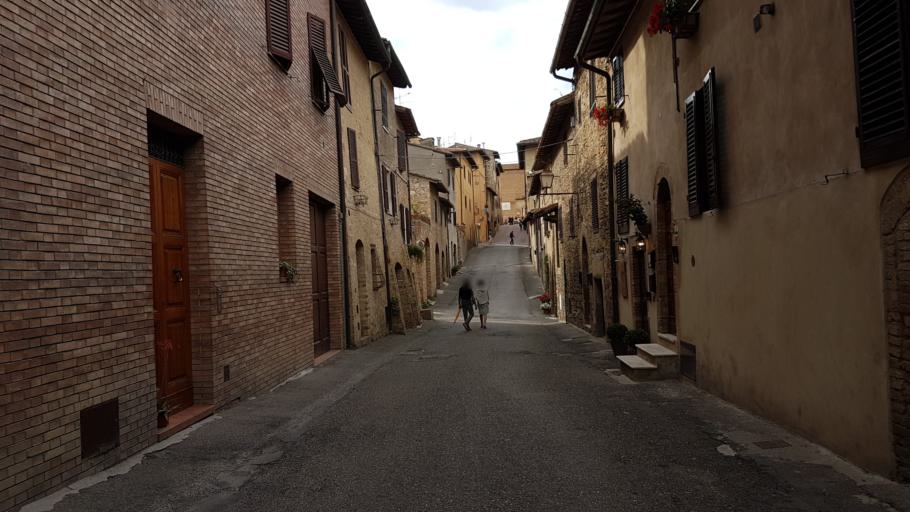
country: IT
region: Tuscany
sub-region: Provincia di Siena
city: San Gimignano
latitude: 43.4693
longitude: 11.0431
